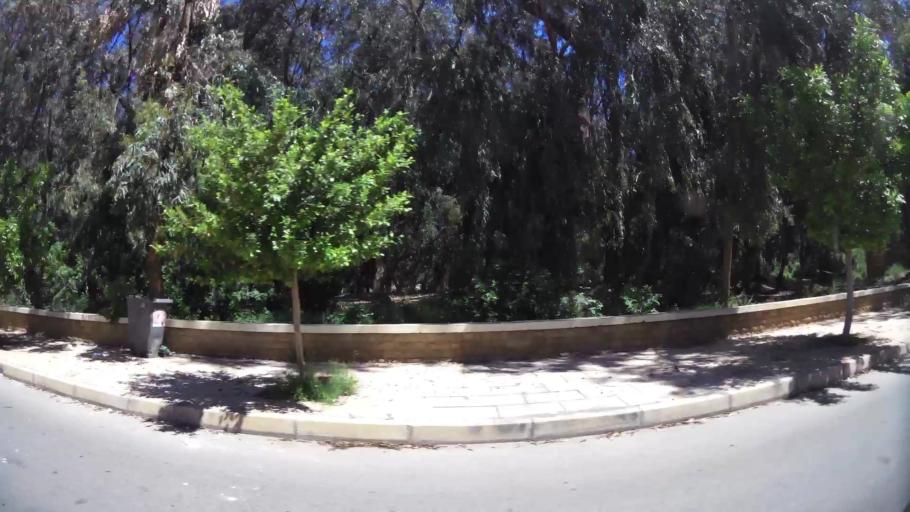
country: MA
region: Oriental
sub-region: Berkane-Taourirt
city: Madagh
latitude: 35.0863
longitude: -2.2362
